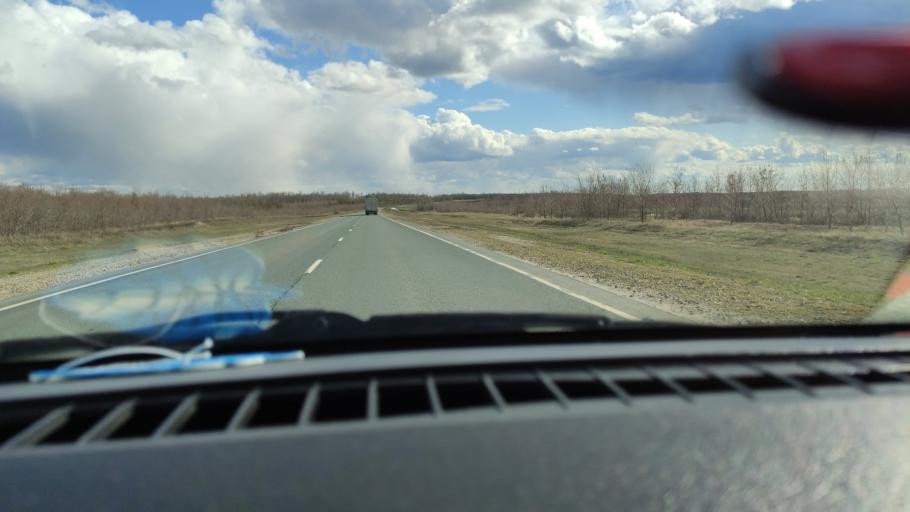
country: RU
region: Saratov
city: Alekseyevka
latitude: 52.2817
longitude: 47.9312
